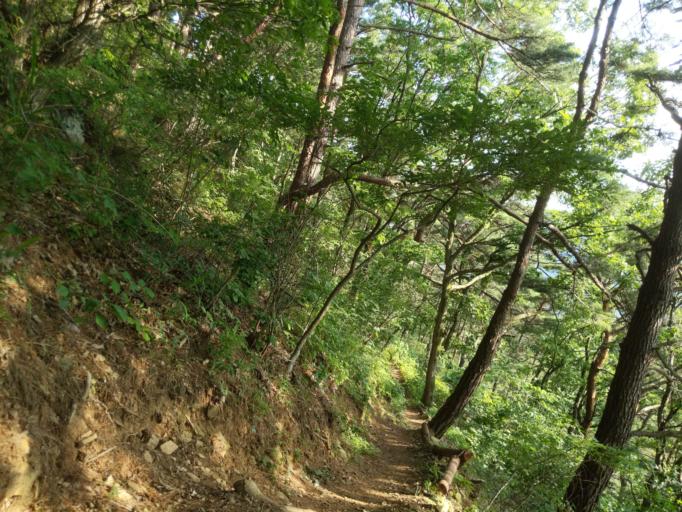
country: KR
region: Daegu
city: Hwawon
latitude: 35.7892
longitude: 128.5405
